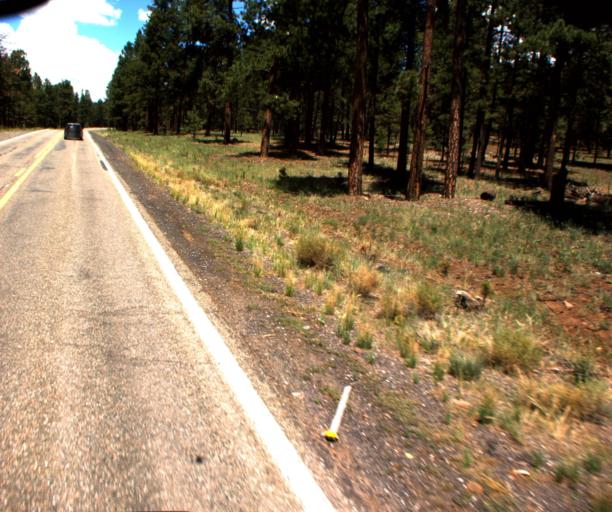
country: US
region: Arizona
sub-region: Coconino County
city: Flagstaff
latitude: 35.2935
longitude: -111.7644
